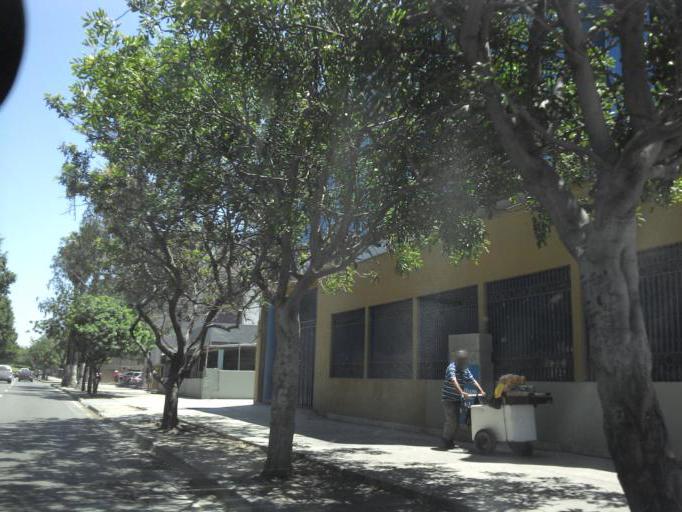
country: MX
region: Baja California
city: Tijuana
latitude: 32.5346
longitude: -117.0212
